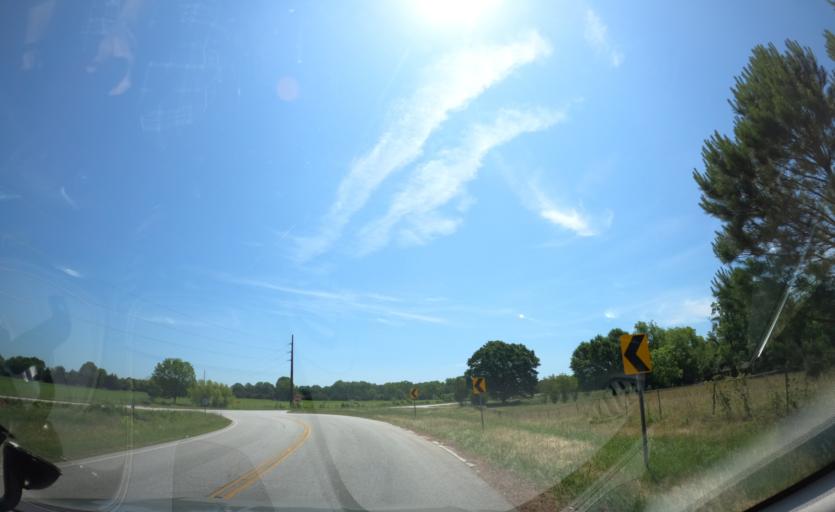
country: US
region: South Carolina
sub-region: Anderson County
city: Iva
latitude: 34.3344
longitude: -82.6862
